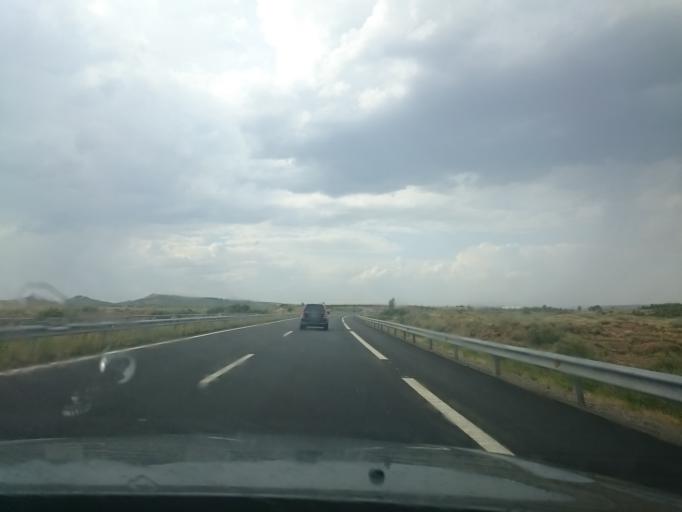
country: ES
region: La Rioja
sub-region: Provincia de La Rioja
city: Aldeanueva de Ebro
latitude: 42.2574
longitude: -1.9222
